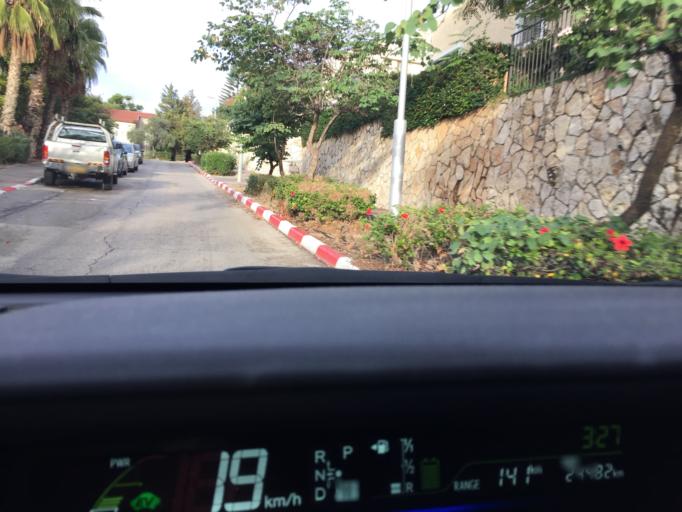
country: PS
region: West Bank
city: Az Zawiyah
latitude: 32.1100
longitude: 35.0316
